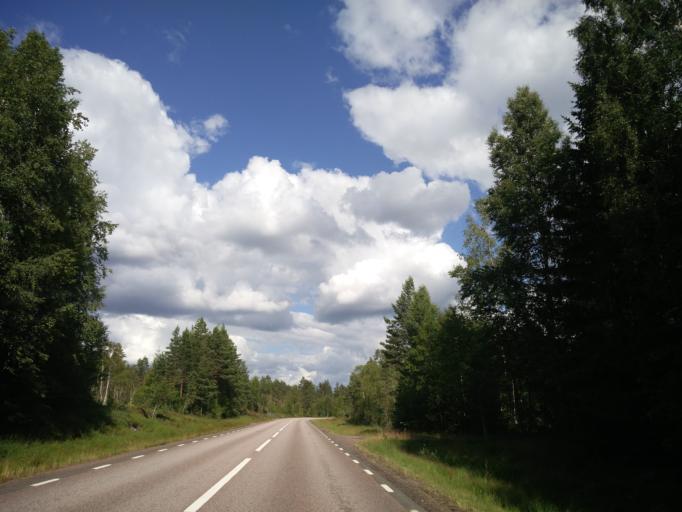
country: SE
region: Vaermland
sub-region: Sunne Kommun
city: Sunne
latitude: 59.6912
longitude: 13.0679
